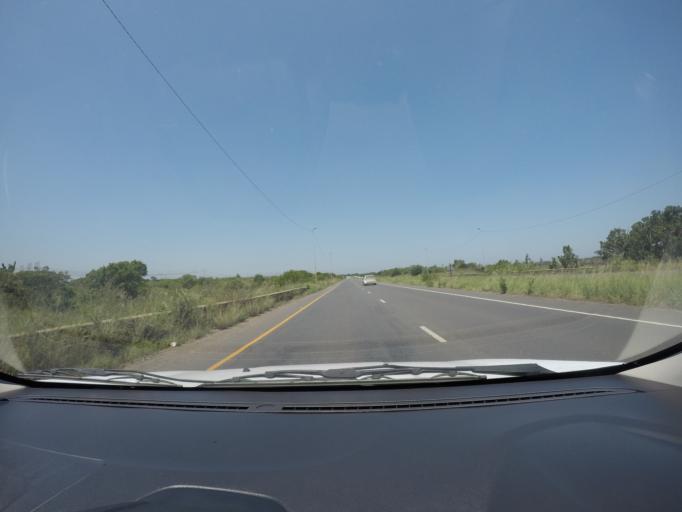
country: ZA
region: KwaZulu-Natal
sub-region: uThungulu District Municipality
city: Richards Bay
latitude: -28.7804
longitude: 31.9916
